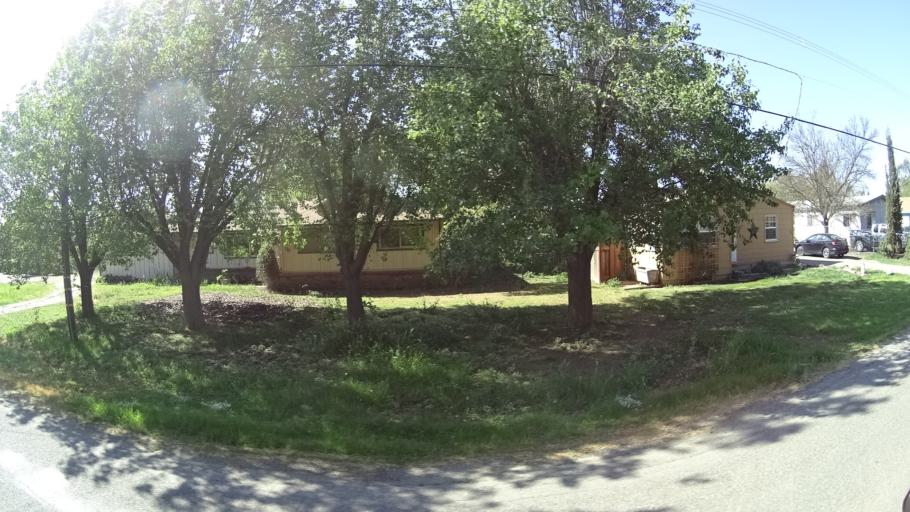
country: US
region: California
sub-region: Glenn County
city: Willows
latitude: 39.5334
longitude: -122.2038
